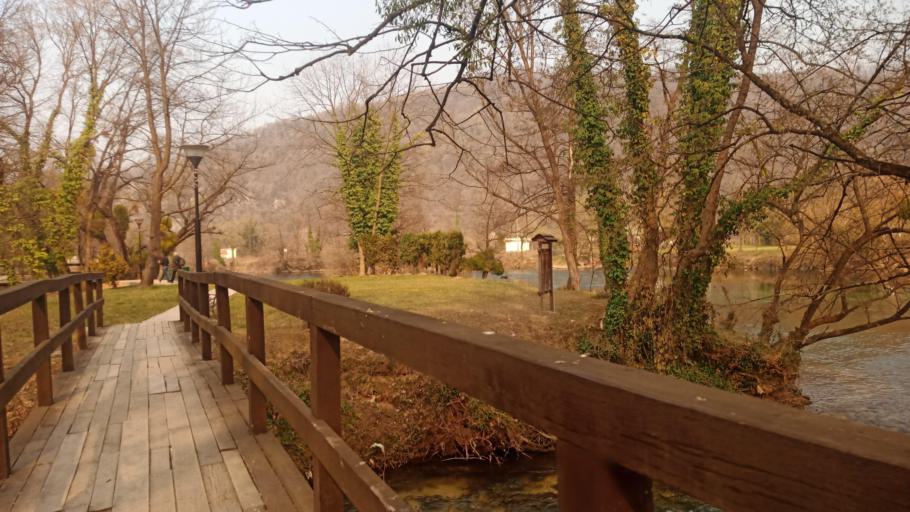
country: BA
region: Federation of Bosnia and Herzegovina
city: Bosanska Krupa
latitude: 44.8883
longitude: 16.1571
